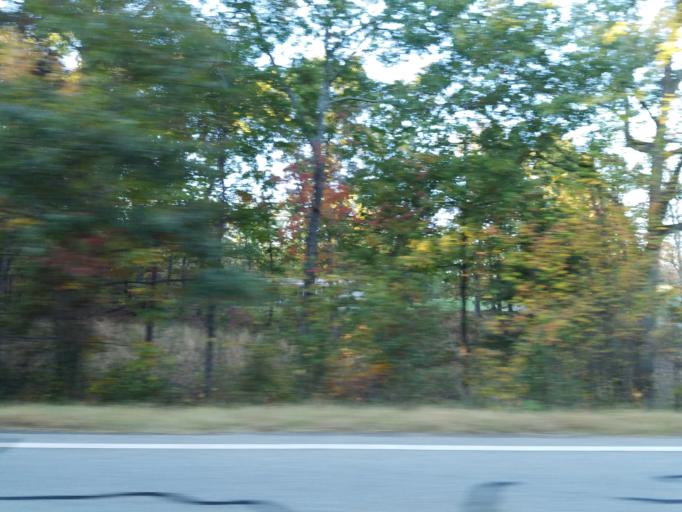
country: US
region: Georgia
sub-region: Dawson County
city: Dawsonville
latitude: 34.5484
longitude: -84.1123
